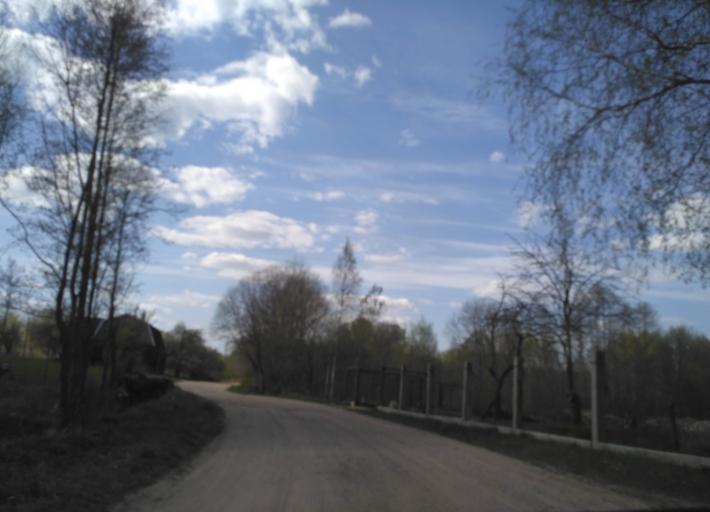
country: BY
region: Minsk
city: Narach
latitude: 54.9890
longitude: 26.5969
